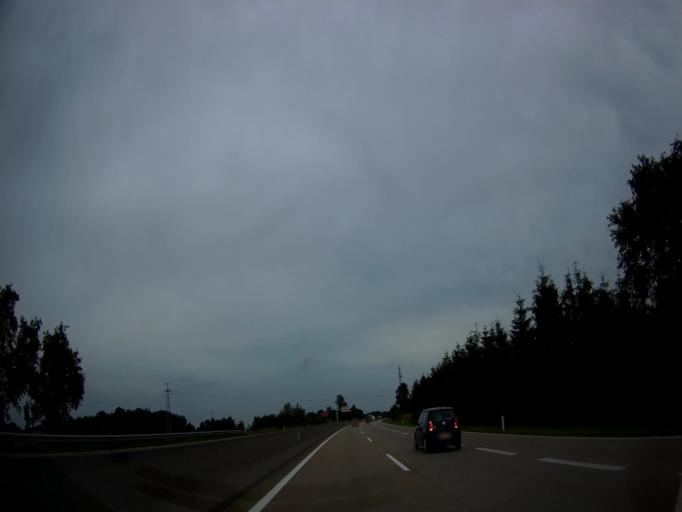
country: AT
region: Upper Austria
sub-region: Wels-Land
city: Sattledt
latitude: 48.0449
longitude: 13.9965
